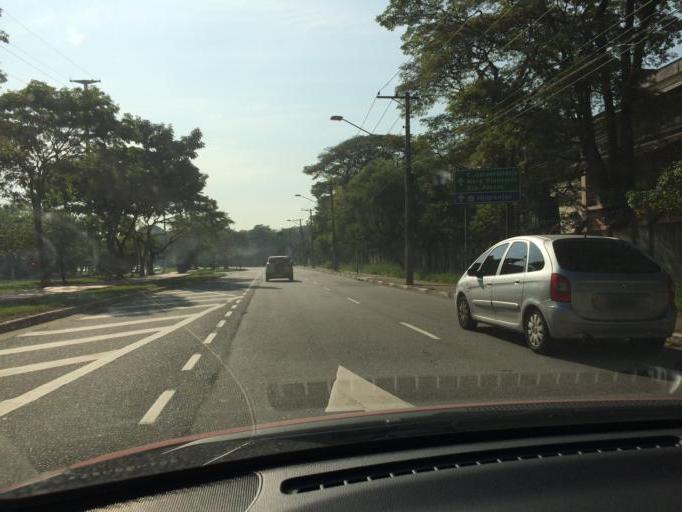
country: BR
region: Sao Paulo
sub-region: Osasco
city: Osasco
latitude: -23.5544
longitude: -46.7348
